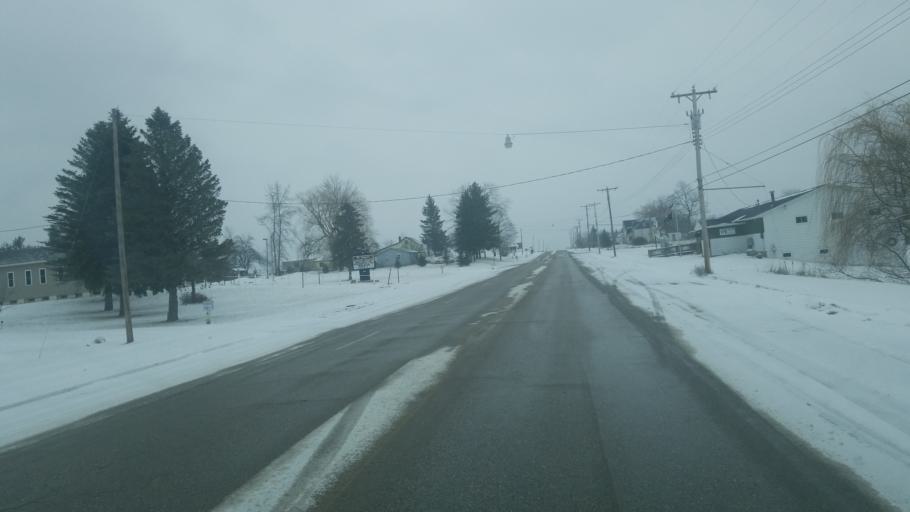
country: US
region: Michigan
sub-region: Osceola County
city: Evart
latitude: 44.1025
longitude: -85.1398
